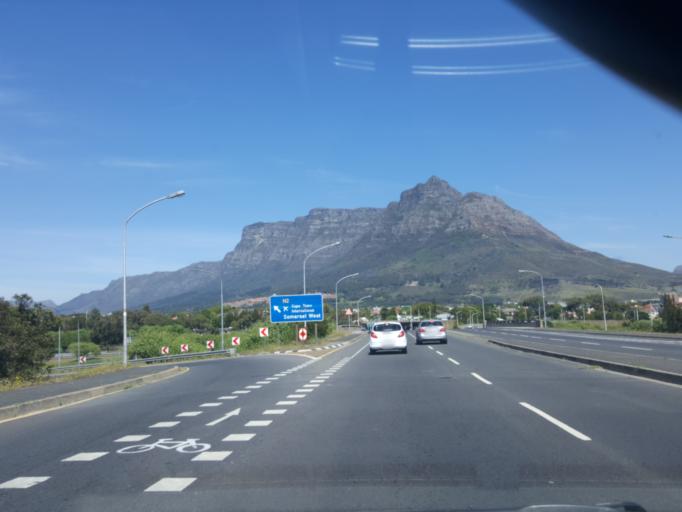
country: ZA
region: Western Cape
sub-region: City of Cape Town
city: Rosebank
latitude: -33.9460
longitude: 18.4898
